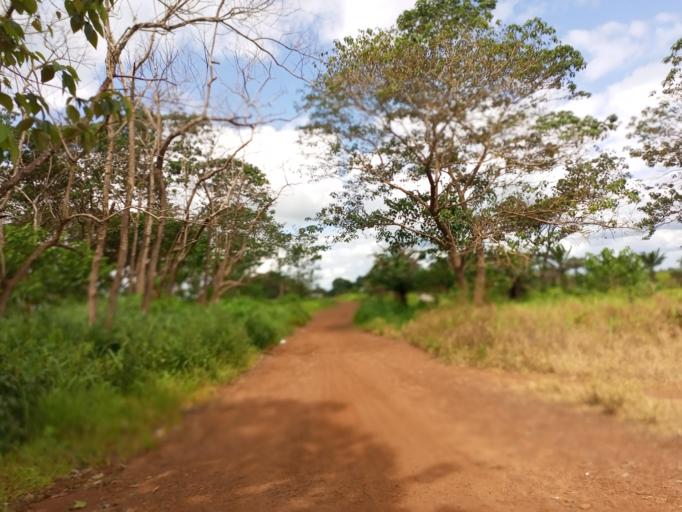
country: SL
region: Northern Province
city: Kamakwie
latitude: 9.5068
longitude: -12.2290
